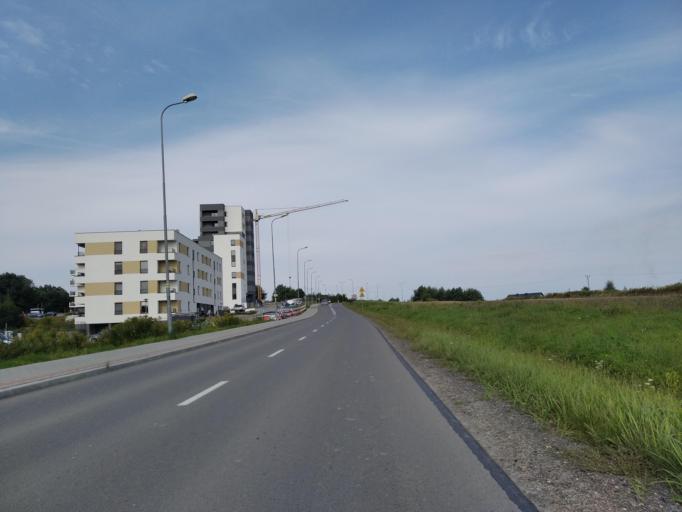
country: PL
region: Subcarpathian Voivodeship
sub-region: Powiat ropczycko-sedziszowski
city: Ropczyce
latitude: 50.0616
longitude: 21.6120
